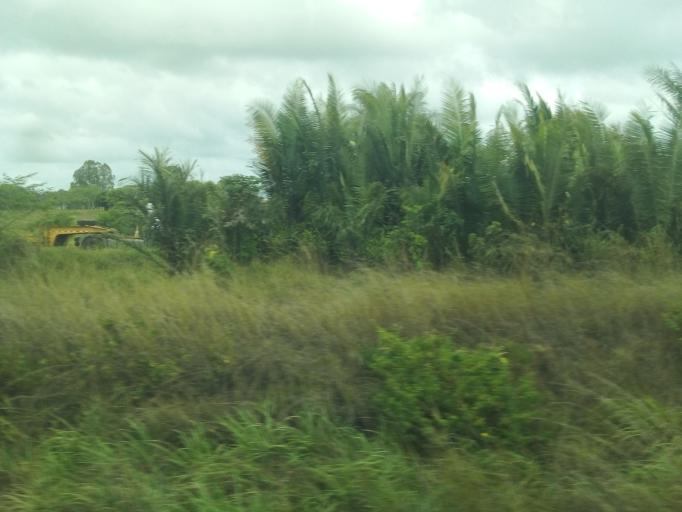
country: BR
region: Maranhao
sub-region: Itapecuru Mirim
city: Itapecuru Mirim
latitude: -3.1914
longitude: -44.3778
